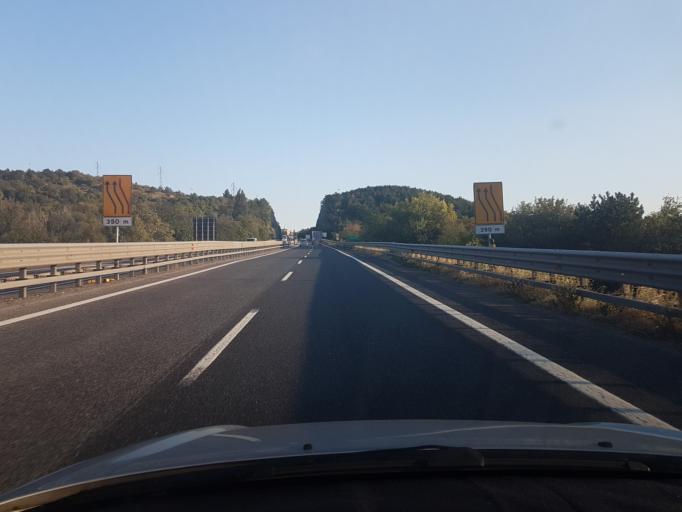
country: IT
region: Friuli Venezia Giulia
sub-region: Provincia di Trieste
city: Duino
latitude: 45.7983
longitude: 13.5840
